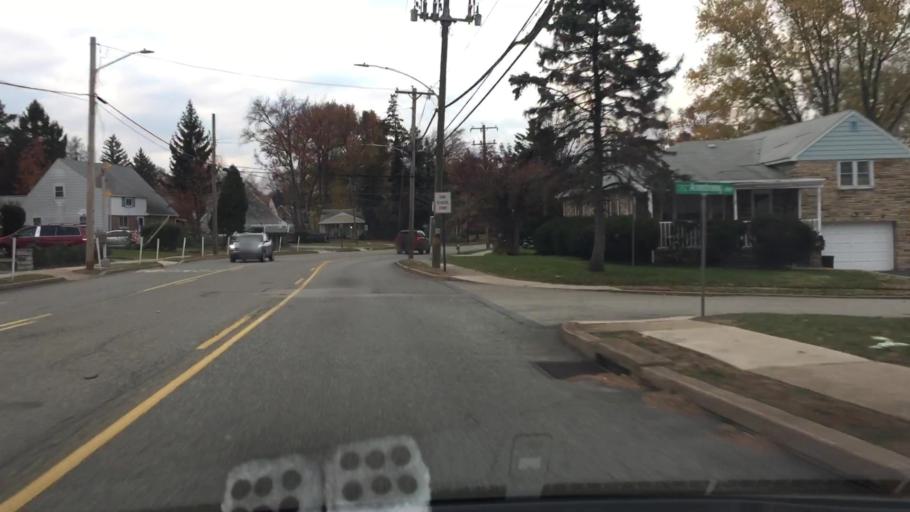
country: US
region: Pennsylvania
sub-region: Delaware County
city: Morton
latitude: 39.9080
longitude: -75.3075
